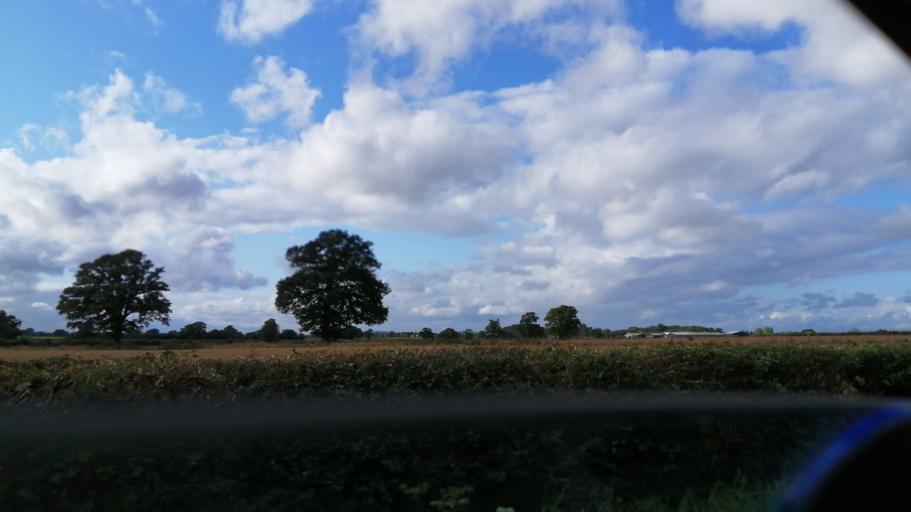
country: GB
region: England
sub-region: Herefordshire
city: Callow
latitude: 52.0007
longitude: -2.7725
